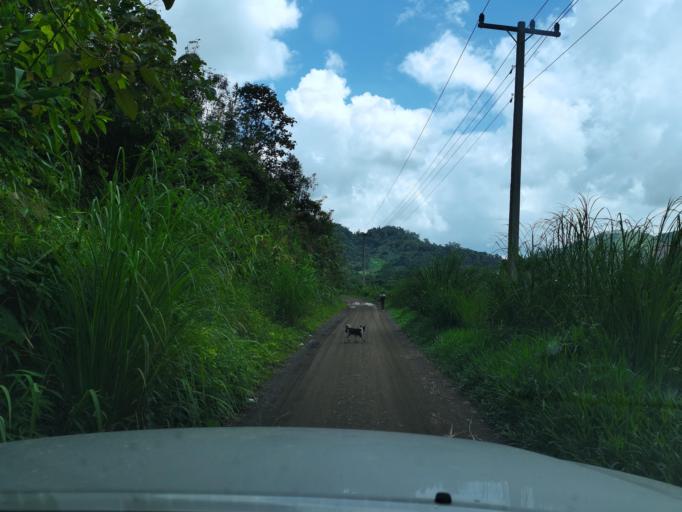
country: LA
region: Loungnamtha
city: Muang Long
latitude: 20.7501
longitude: 101.0183
